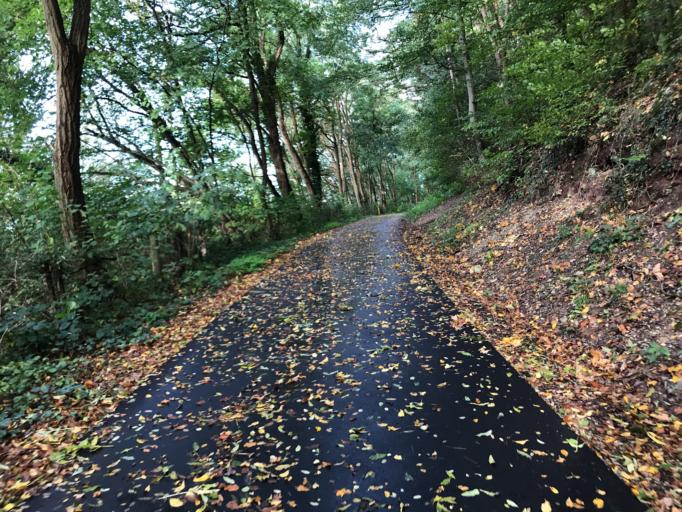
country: DE
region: Hesse
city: Witzenhausen
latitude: 51.3332
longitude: 9.8619
